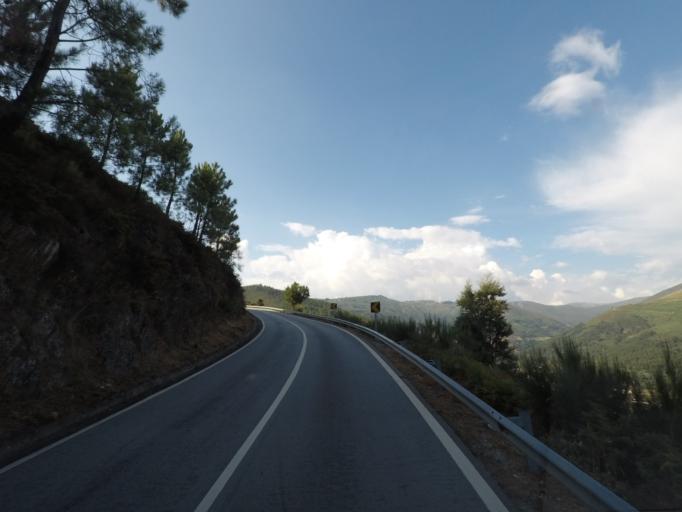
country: PT
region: Vila Real
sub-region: Mesao Frio
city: Mesao Frio
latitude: 41.1768
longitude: -7.9272
